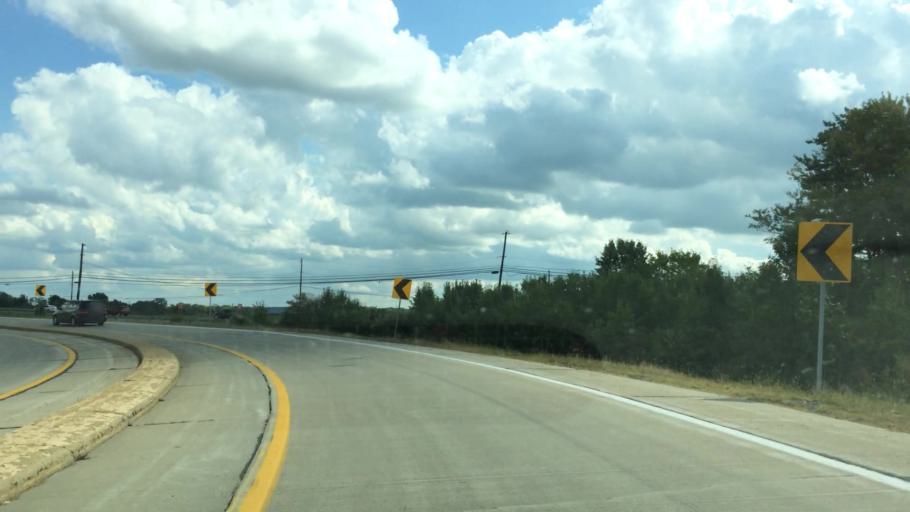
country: US
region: Ohio
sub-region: Wood County
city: Rossford
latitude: 41.5658
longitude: -83.5775
